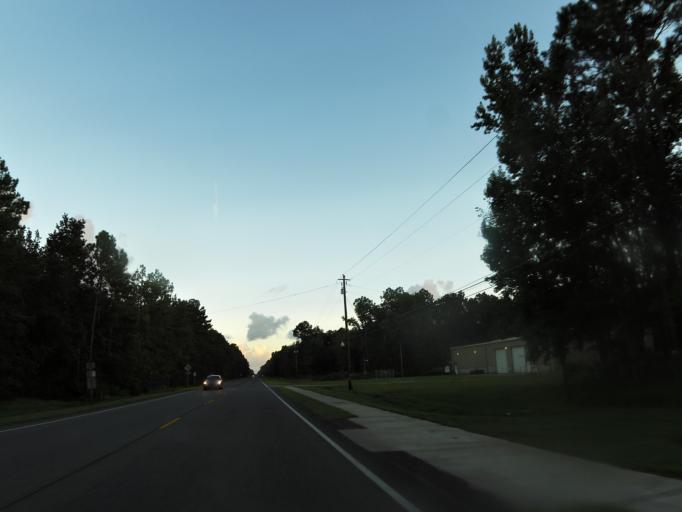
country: US
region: Georgia
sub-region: Camden County
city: Woodbine
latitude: 30.9502
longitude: -81.7201
